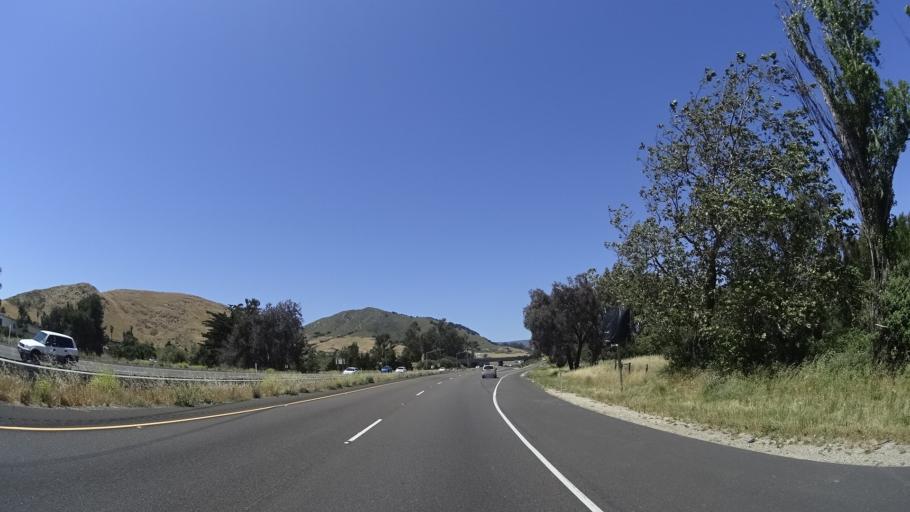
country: US
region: California
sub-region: San Luis Obispo County
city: San Luis Obispo
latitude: 35.2629
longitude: -120.6735
